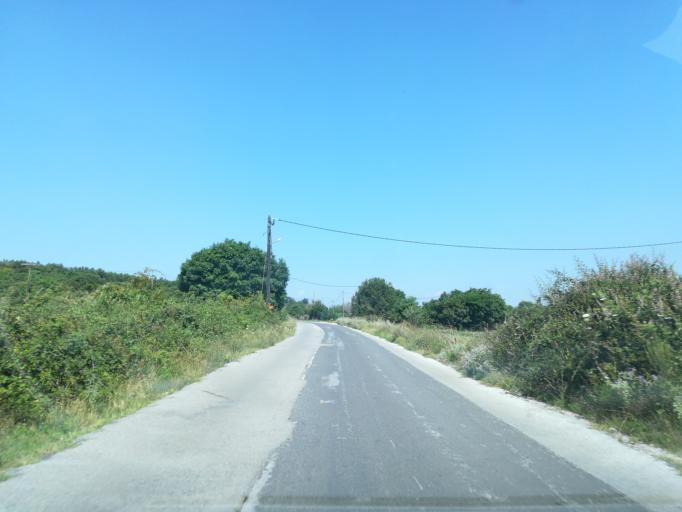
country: GR
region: Central Macedonia
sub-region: Nomos Thessalonikis
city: Asvestochori
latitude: 40.6326
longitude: 23.0274
